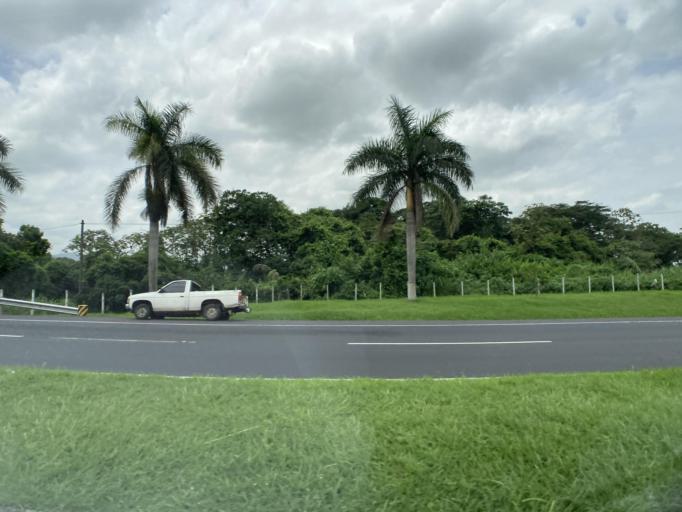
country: GT
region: Escuintla
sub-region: Municipio de Escuintla
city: Escuintla
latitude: 14.3443
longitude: -90.7901
